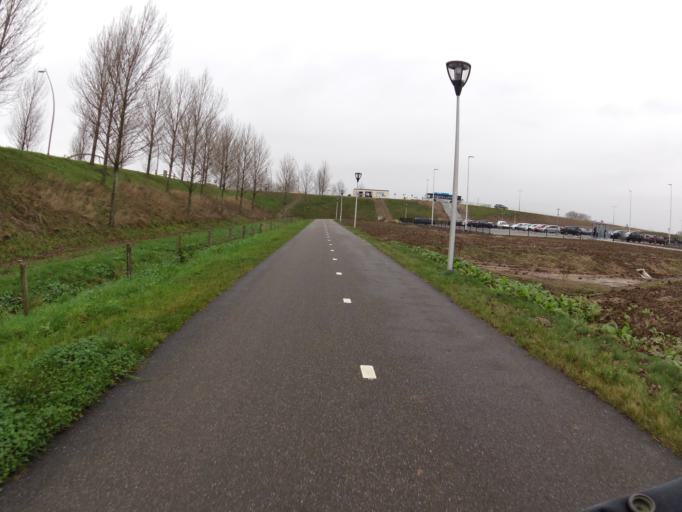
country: NL
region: Gelderland
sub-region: Gemeente Overbetuwe
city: Oosterhout
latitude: 51.8813
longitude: 5.8599
